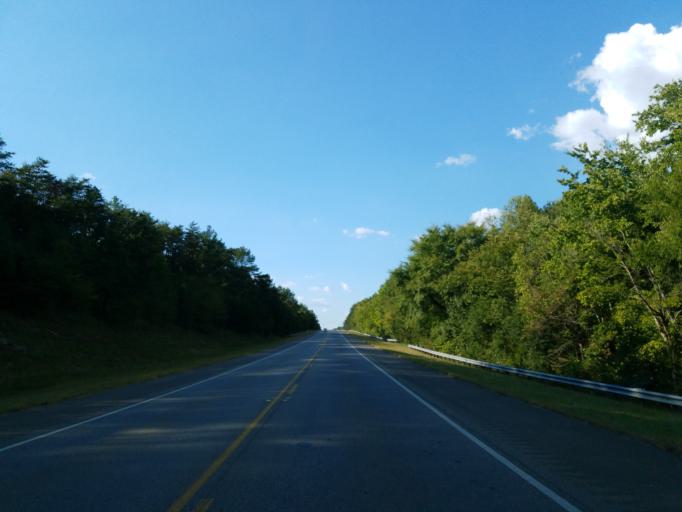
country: US
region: Georgia
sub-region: Murray County
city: Chatsworth
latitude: 34.6787
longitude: -84.7270
